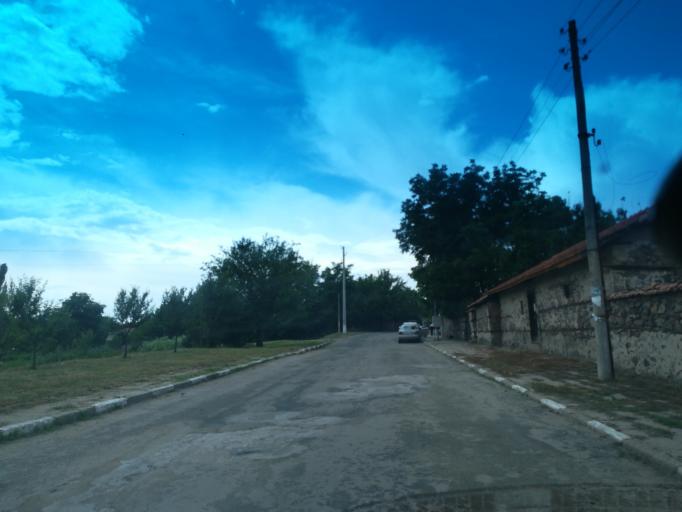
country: BG
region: Khaskovo
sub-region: Obshtina Mineralni Bani
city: Mineralni Bani
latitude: 41.9947
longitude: 25.2278
